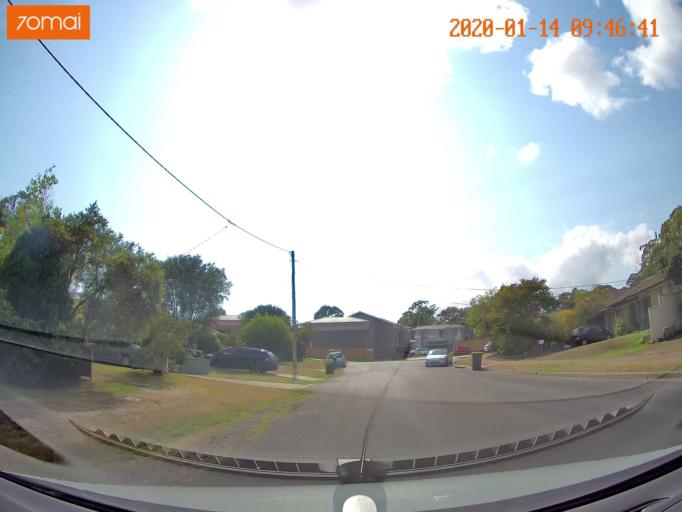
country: AU
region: New South Wales
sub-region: Lake Macquarie Shire
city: Dora Creek
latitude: -33.1099
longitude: 151.5297
